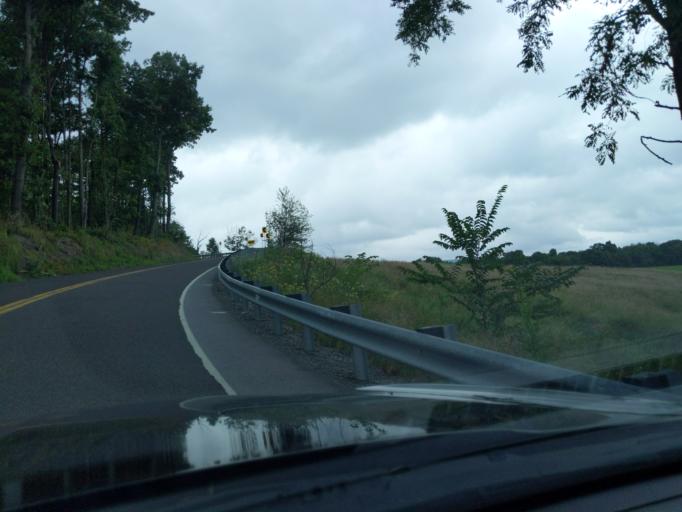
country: US
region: Pennsylvania
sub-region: Blair County
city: Claysburg
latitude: 40.3557
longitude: -78.5085
